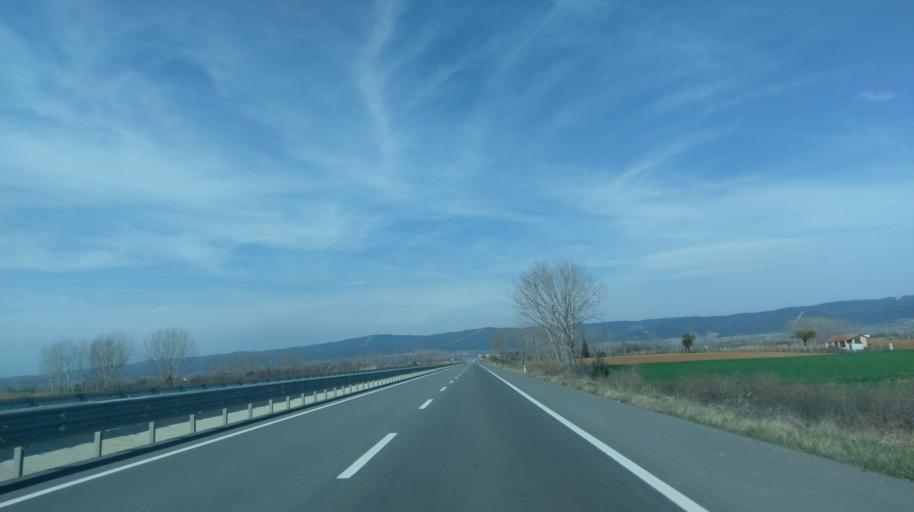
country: TR
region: Canakkale
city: Evrese
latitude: 40.6525
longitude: 26.8319
